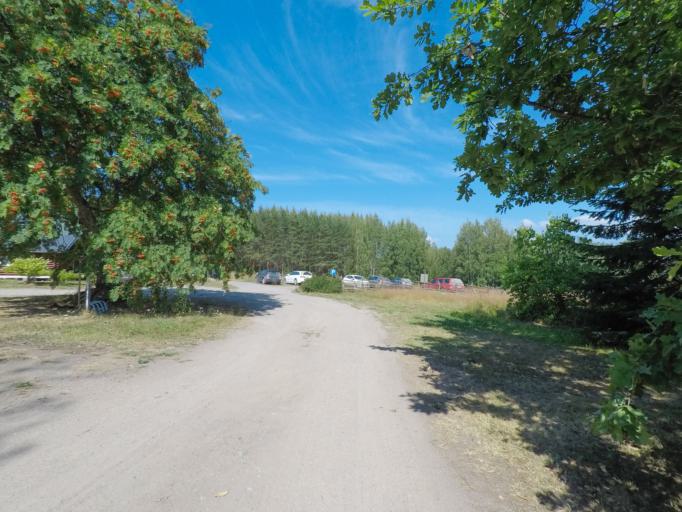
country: FI
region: Southern Savonia
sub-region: Mikkeli
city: Puumala
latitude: 61.4274
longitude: 28.0133
